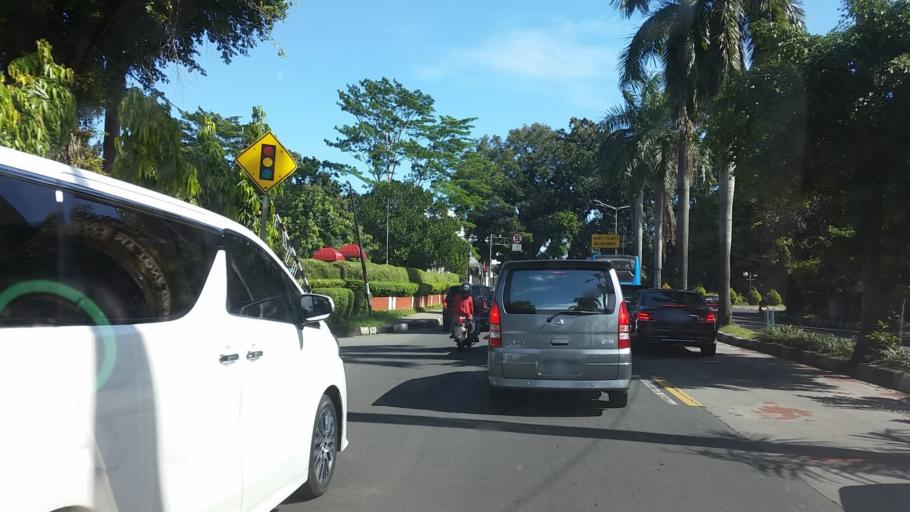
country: ID
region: Banten
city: South Tangerang
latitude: -6.2813
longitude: 106.7804
